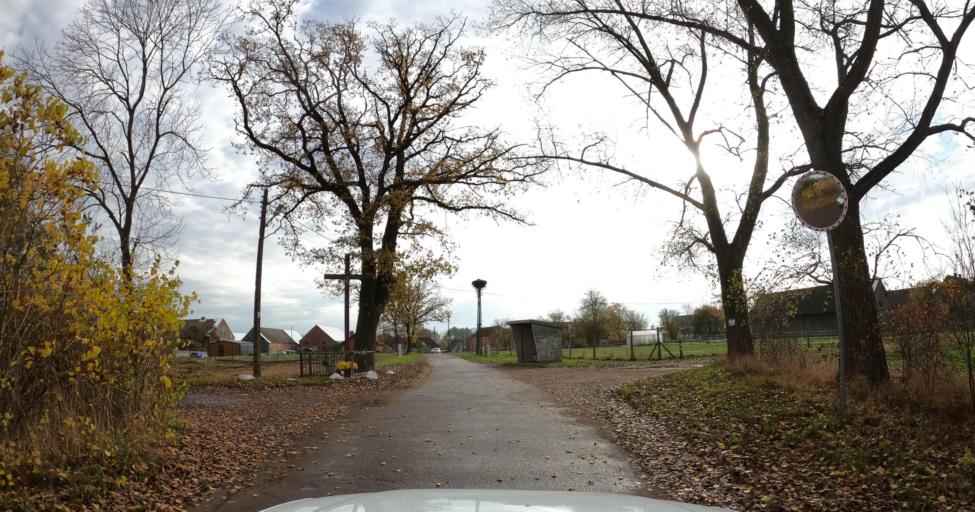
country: PL
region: West Pomeranian Voivodeship
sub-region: Powiat kamienski
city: Kamien Pomorski
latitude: 53.9938
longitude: 14.8424
